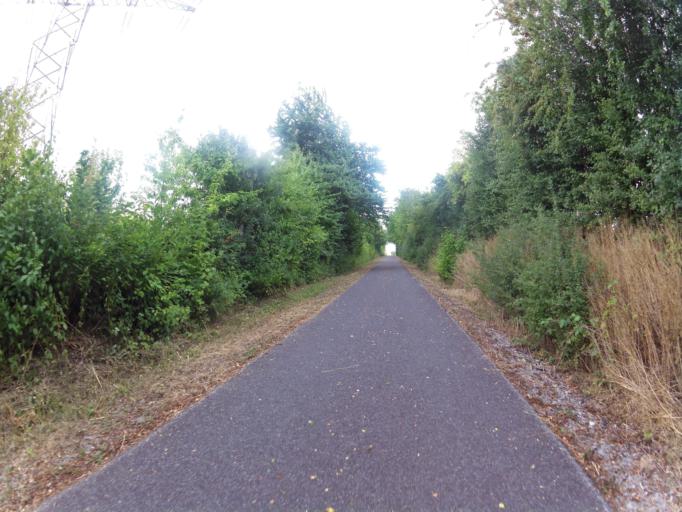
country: DE
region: Bavaria
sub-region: Regierungsbezirk Unterfranken
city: Sonderhofen
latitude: 49.5854
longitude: 10.0086
